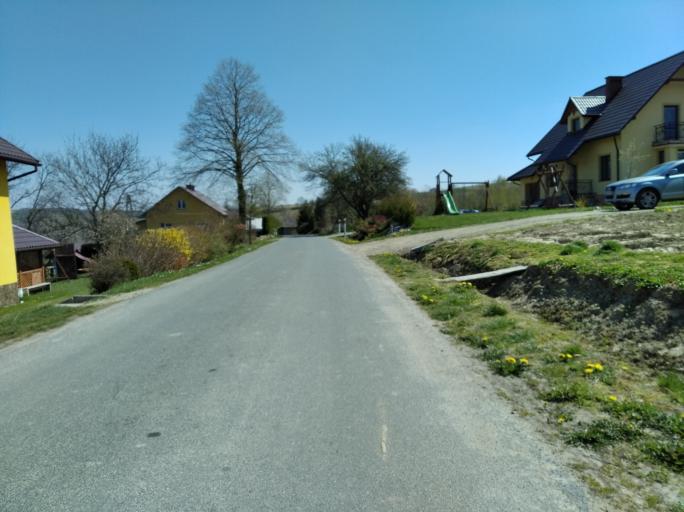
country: PL
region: Subcarpathian Voivodeship
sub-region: Powiat strzyzowski
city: Wisniowa
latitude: 49.9086
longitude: 21.6888
